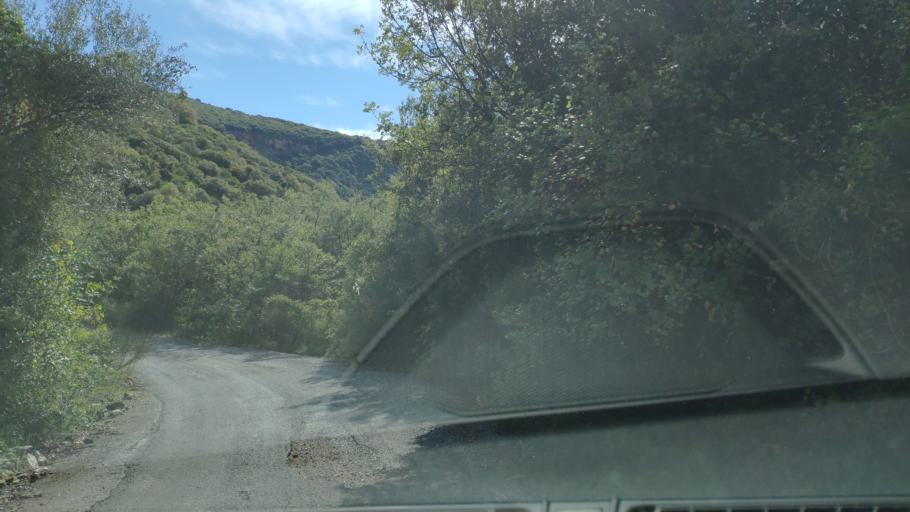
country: GR
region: Peloponnese
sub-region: Nomos Arkadias
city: Dimitsana
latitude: 37.5378
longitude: 22.0516
